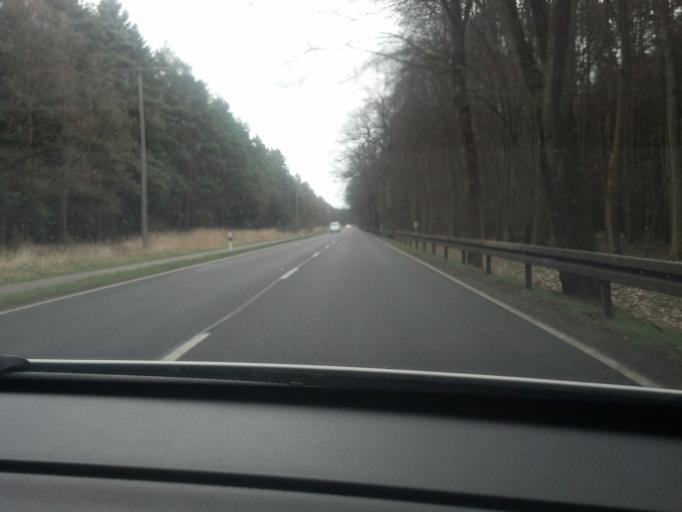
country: DE
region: Mecklenburg-Vorpommern
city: Wesenberg
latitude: 53.2712
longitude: 12.8687
